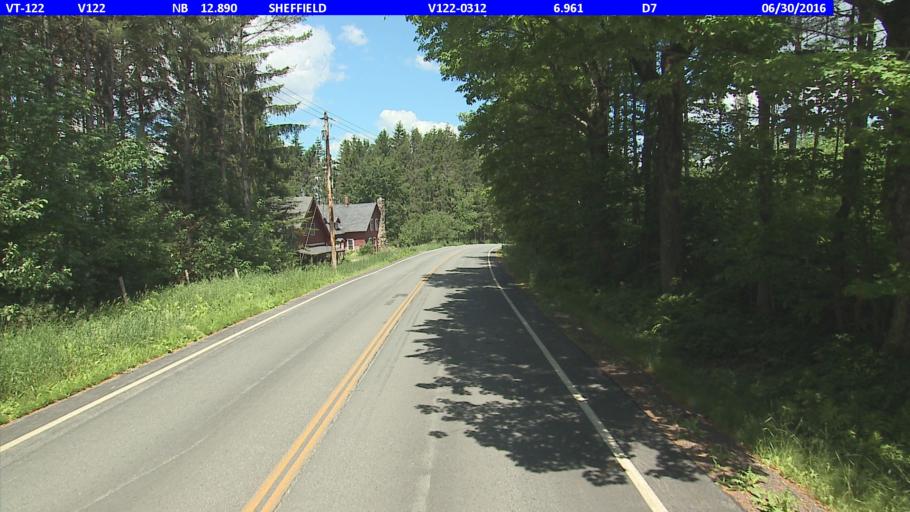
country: US
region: Vermont
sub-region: Caledonia County
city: Lyndonville
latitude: 44.6684
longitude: -72.1610
